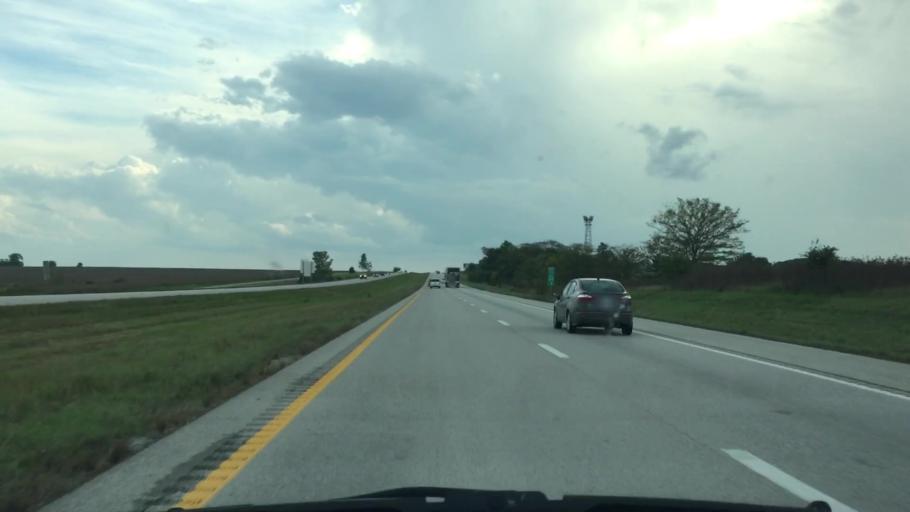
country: US
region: Missouri
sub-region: Clinton County
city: Cameron
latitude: 39.8418
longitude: -94.1821
